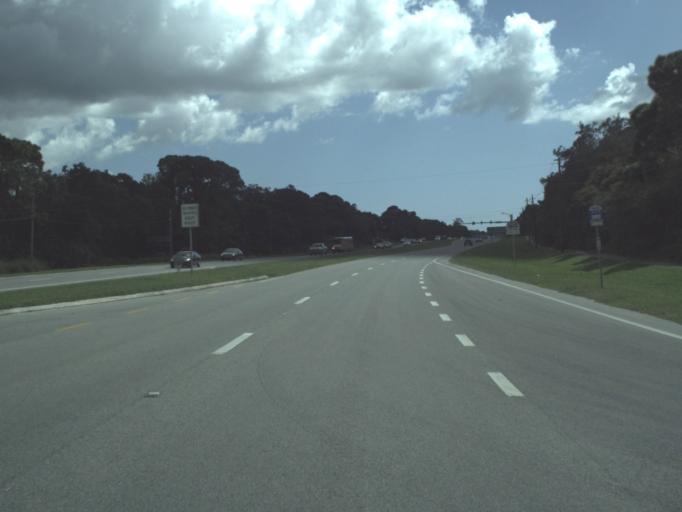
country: US
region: Florida
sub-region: Sarasota County
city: Vamo
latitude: 27.2183
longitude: -82.4905
